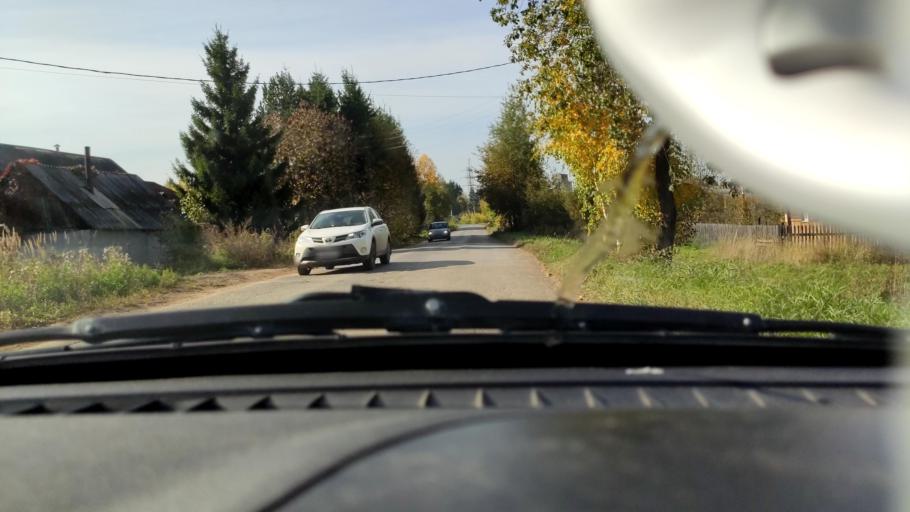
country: RU
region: Perm
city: Overyata
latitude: 58.0729
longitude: 55.8864
